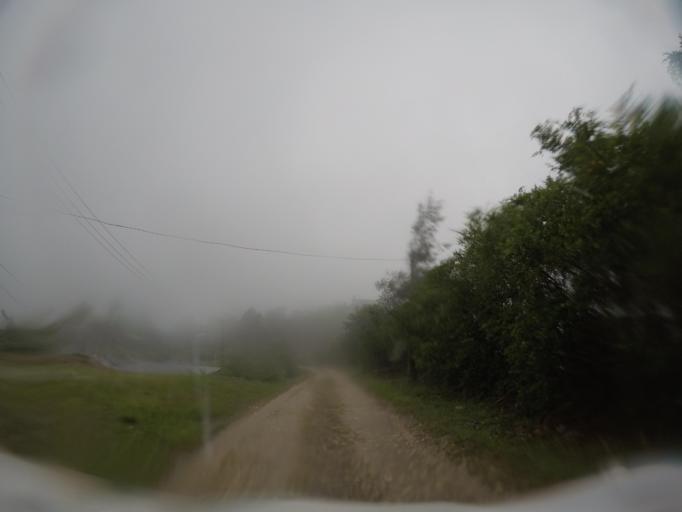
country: TL
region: Baucau
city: Venilale
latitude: -8.6404
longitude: 126.4064
